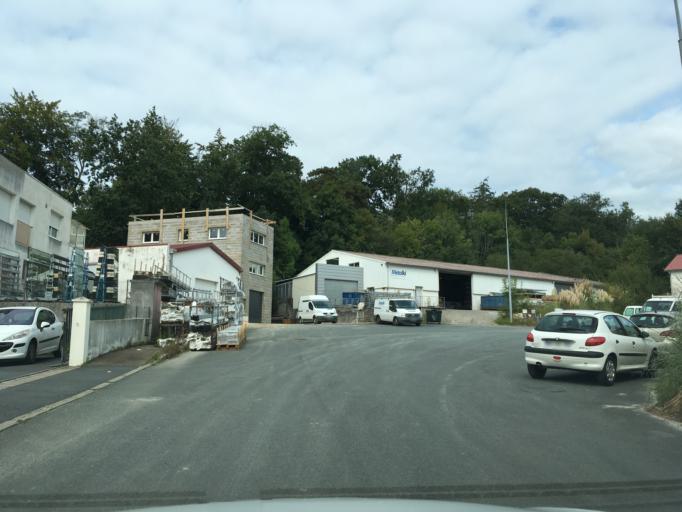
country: FR
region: Aquitaine
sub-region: Departement des Pyrenees-Atlantiques
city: Biarritz
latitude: 43.4638
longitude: -1.5417
